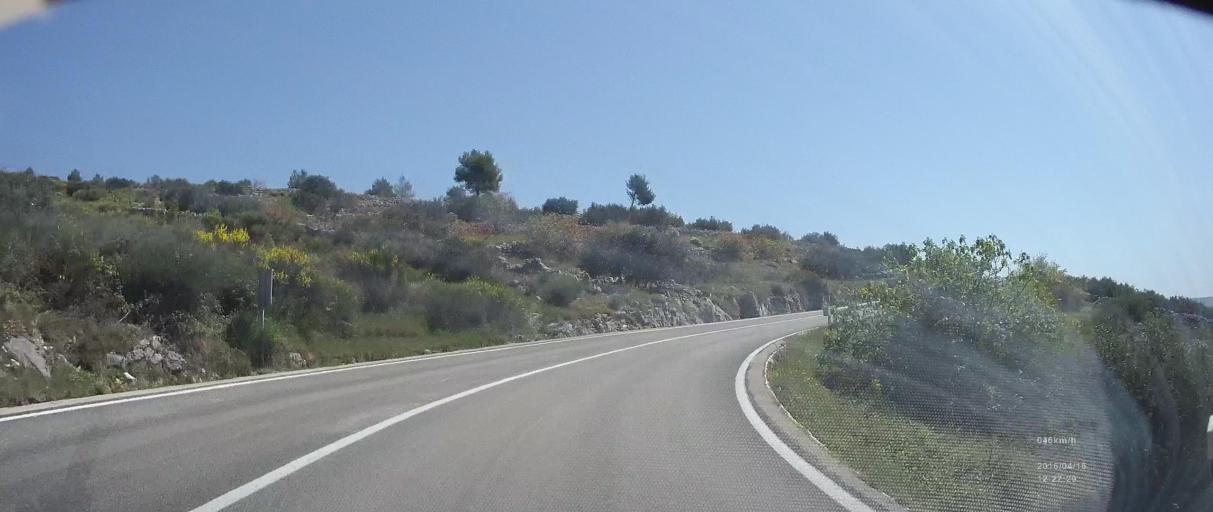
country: HR
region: Splitsko-Dalmatinska
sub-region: Grad Trogir
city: Trogir
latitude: 43.5204
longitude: 16.2035
